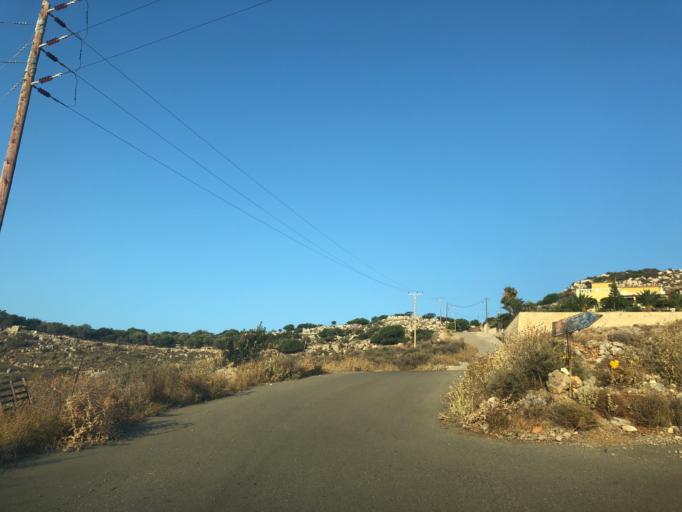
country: GR
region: Crete
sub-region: Nomos Rethymnis
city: Atsipopoulon
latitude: 35.3592
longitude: 24.3933
